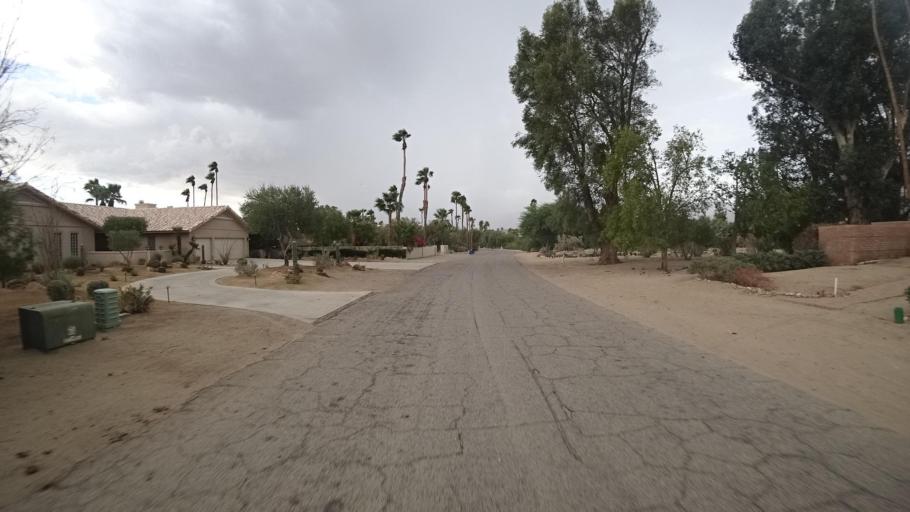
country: US
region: California
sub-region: San Diego County
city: Borrego Springs
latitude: 33.2924
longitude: -116.3880
